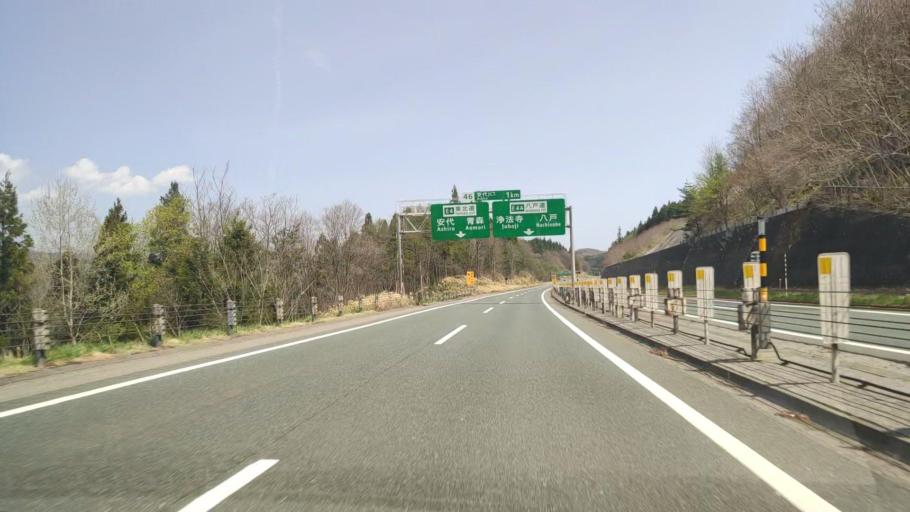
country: JP
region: Iwate
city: Ichinohe
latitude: 40.0939
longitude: 141.0523
